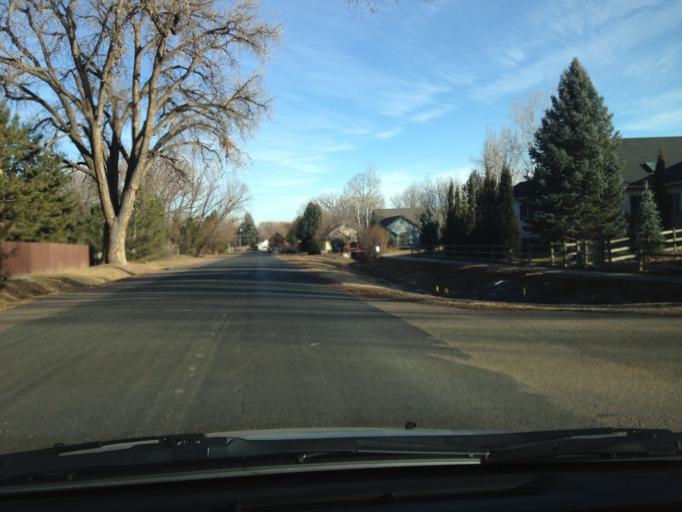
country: US
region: Colorado
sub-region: Boulder County
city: Niwot
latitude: 40.1052
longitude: -105.1624
